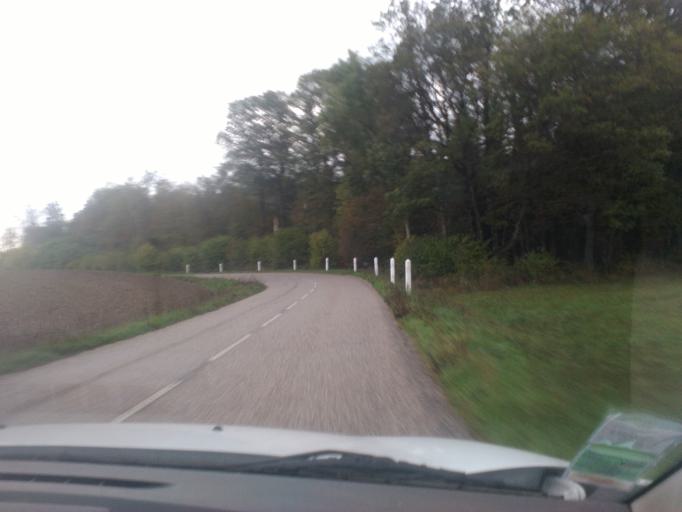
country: FR
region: Lorraine
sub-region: Departement des Vosges
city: Thaon-les-Vosges
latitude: 48.2882
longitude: 6.4495
